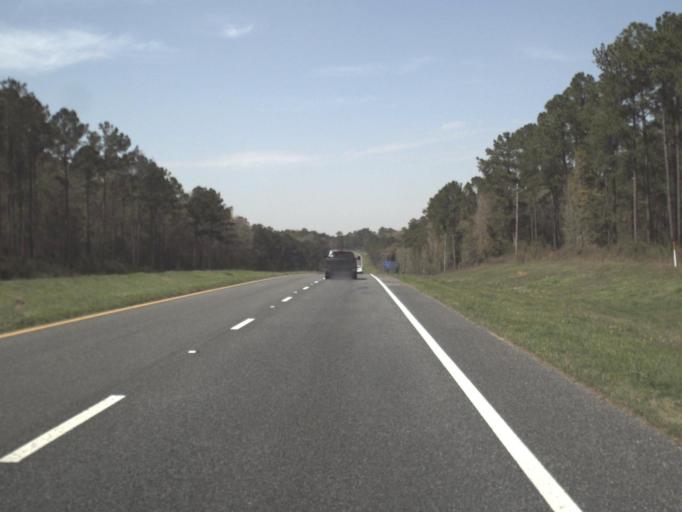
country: US
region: Florida
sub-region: Gadsden County
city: Midway
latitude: 30.5418
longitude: -84.4806
